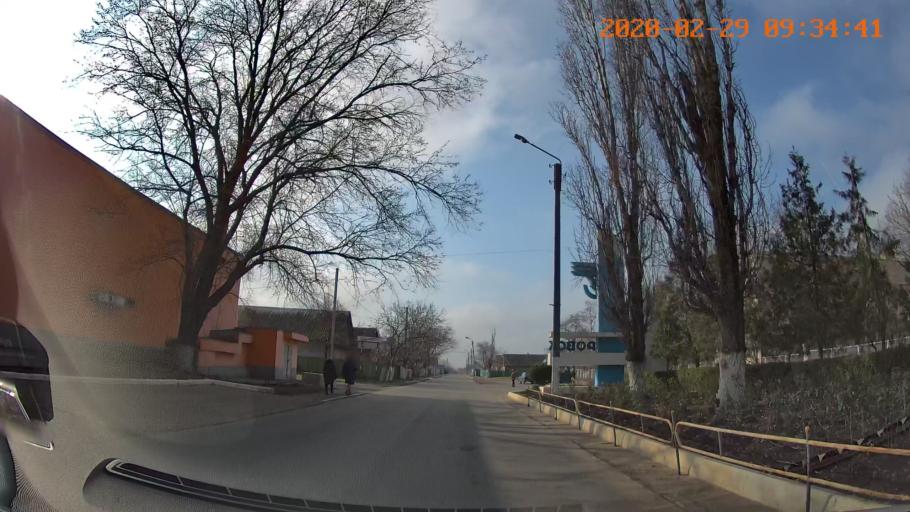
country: MD
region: Telenesti
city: Dnestrovsc
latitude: 46.6225
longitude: 29.9031
